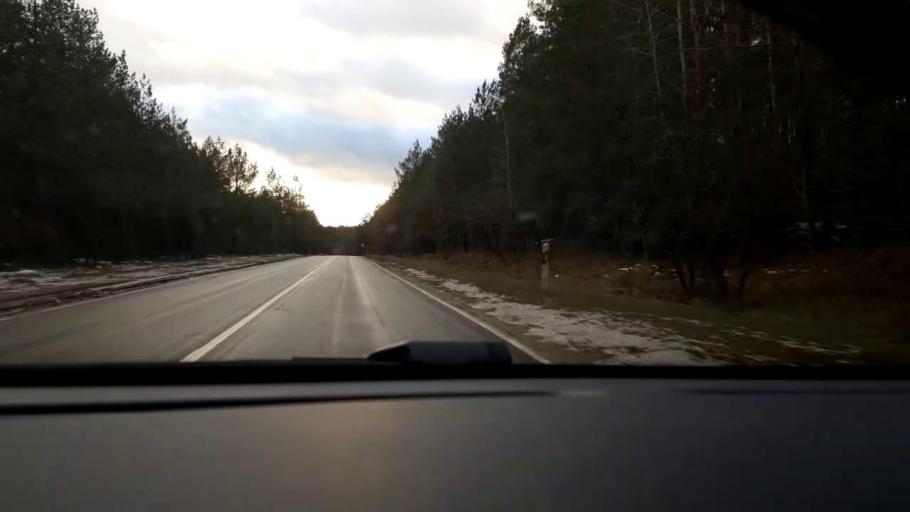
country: LT
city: Nemencine
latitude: 54.7918
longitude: 25.3887
